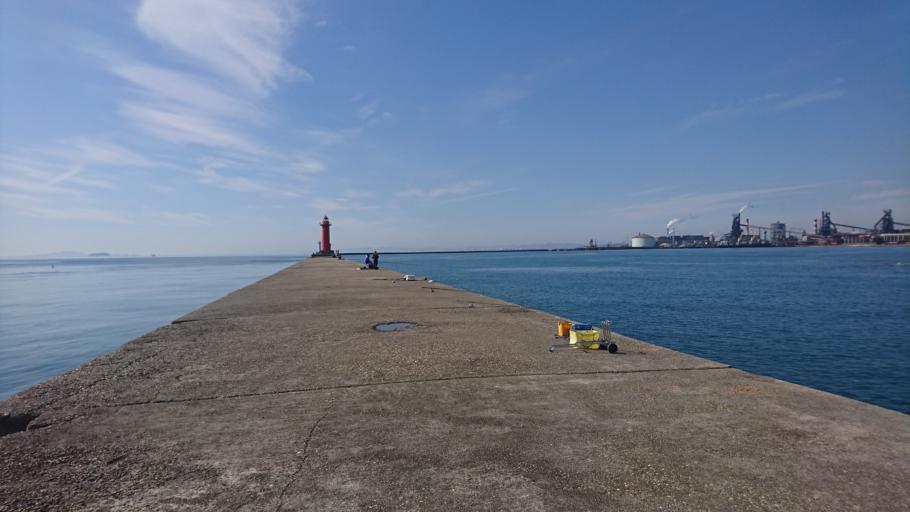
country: JP
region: Hyogo
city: Kakogawacho-honmachi
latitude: 34.6969
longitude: 134.8391
